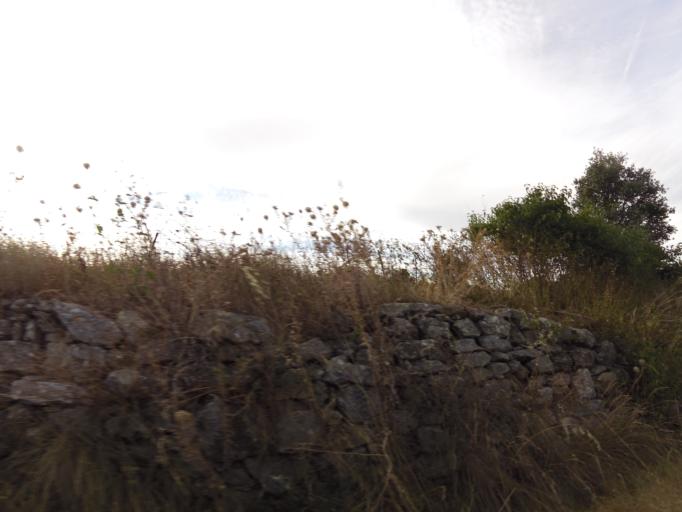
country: FR
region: Languedoc-Roussillon
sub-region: Departement du Gard
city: Saint-Mamert-du-Gard
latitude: 43.8816
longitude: 4.1831
